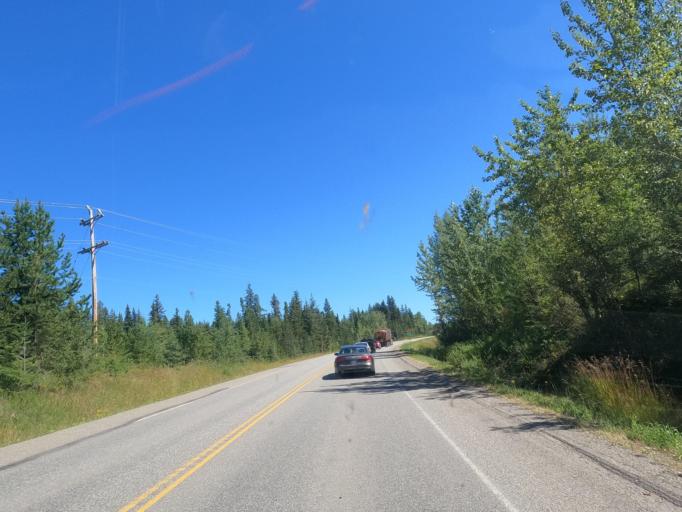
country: CA
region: British Columbia
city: Quesnel
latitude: 53.0629
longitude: -122.4448
